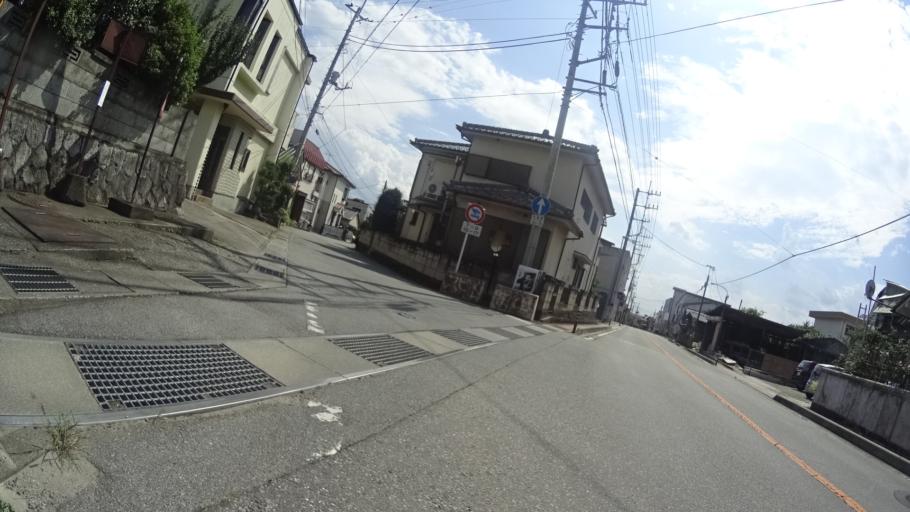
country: JP
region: Yamanashi
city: Enzan
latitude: 35.7110
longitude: 138.7328
